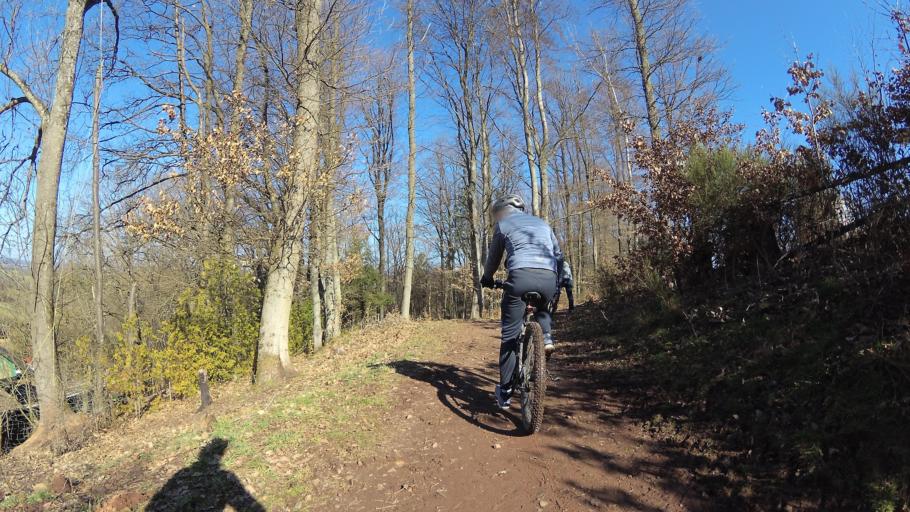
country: DE
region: Saarland
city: Ottweiler
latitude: 49.4059
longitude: 7.1904
